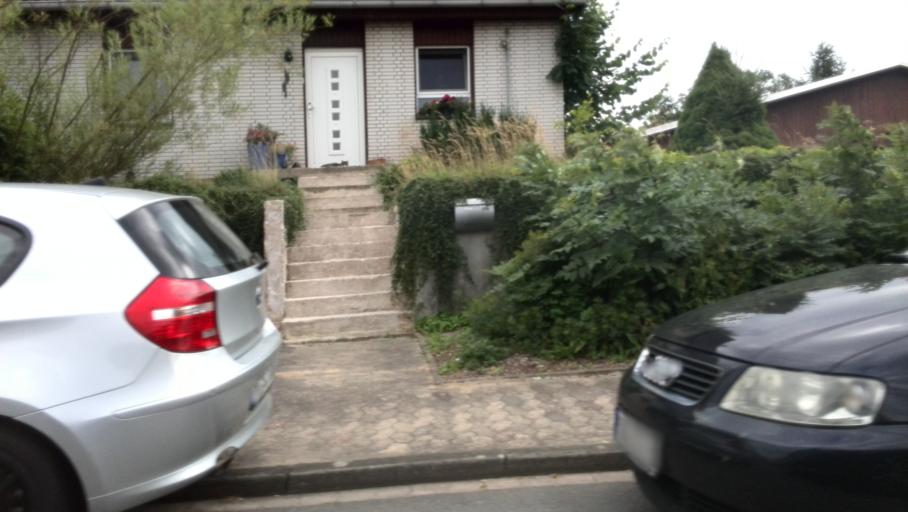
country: DE
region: Lower Saxony
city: Haverlah
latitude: 52.0713
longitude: 10.1732
